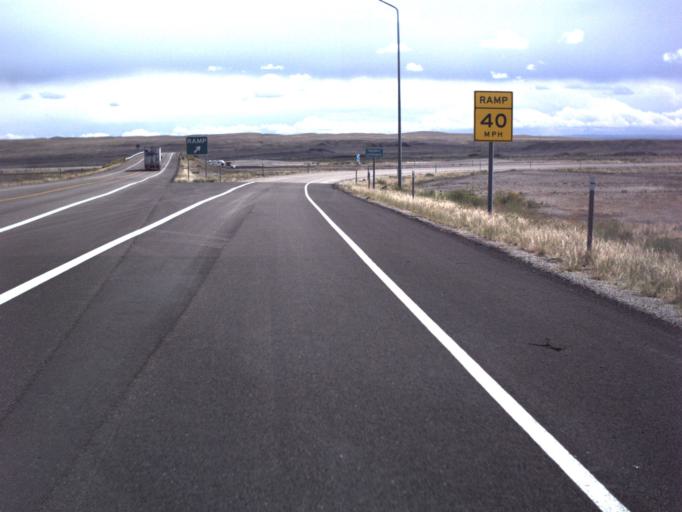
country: US
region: Utah
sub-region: Carbon County
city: East Carbon City
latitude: 38.9848
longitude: -110.2385
